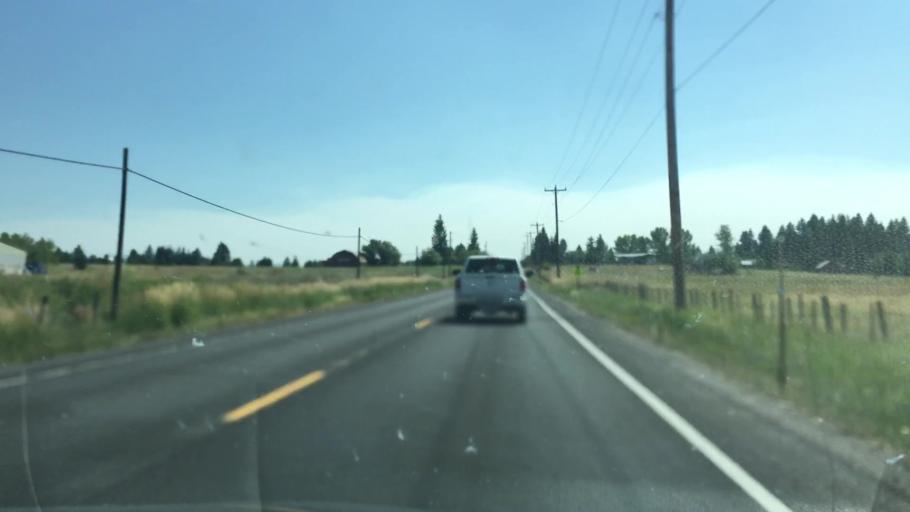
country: US
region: Idaho
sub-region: Valley County
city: McCall
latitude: 44.8755
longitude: -116.0908
